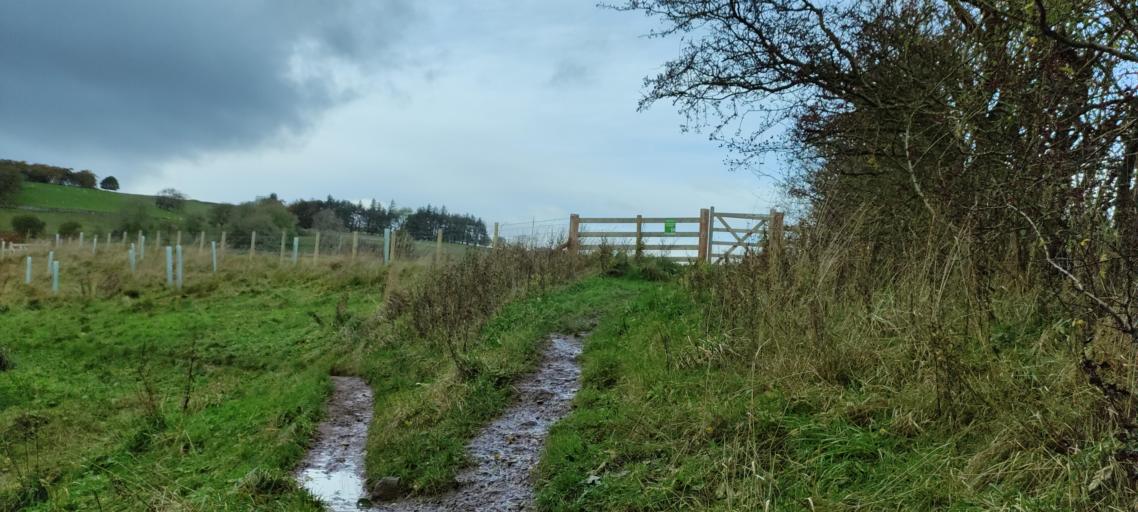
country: GB
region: England
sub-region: Cumbria
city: Wigton
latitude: 54.7491
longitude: -3.0619
